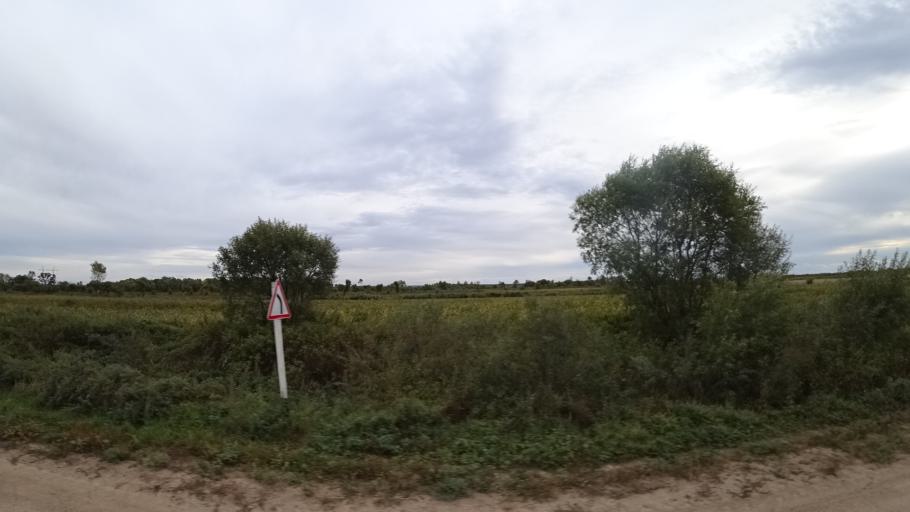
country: RU
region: Amur
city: Arkhara
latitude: 49.4300
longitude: 130.2460
